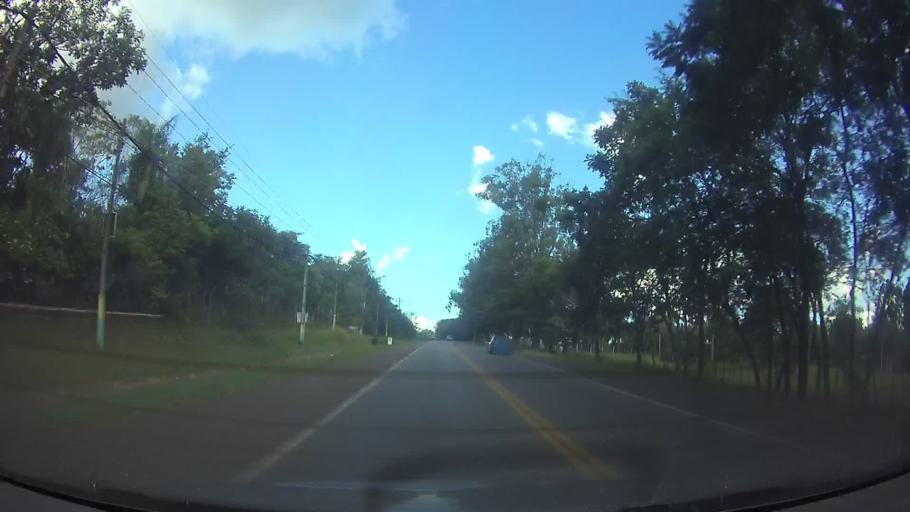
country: PY
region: Cordillera
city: Caacupe
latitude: -25.3861
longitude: -57.1211
